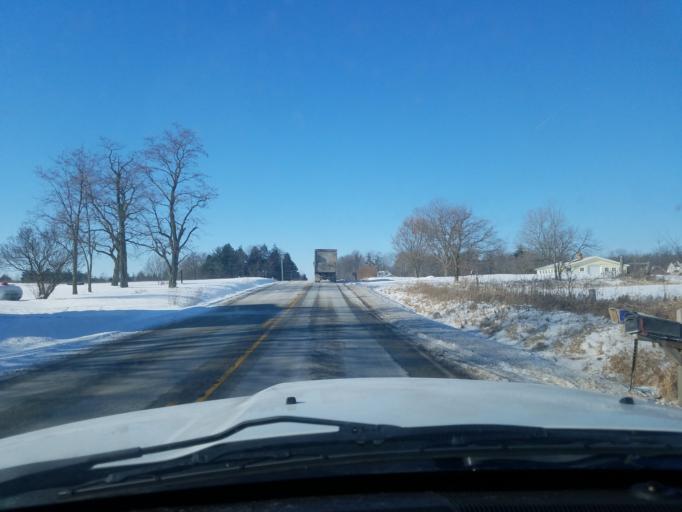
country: US
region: Indiana
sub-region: Noble County
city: Avilla
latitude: 41.3948
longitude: -85.2532
